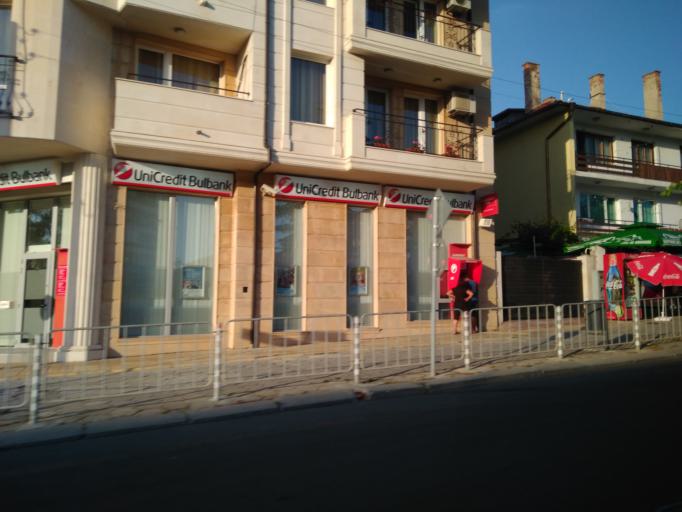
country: BG
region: Burgas
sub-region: Obshtina Nesebur
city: Nesebar
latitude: 42.6639
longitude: 27.7168
